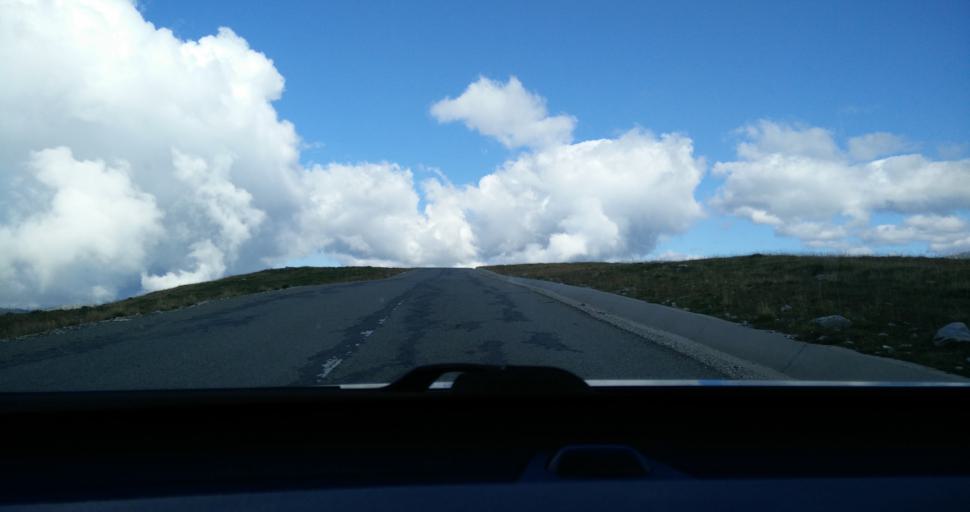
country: RO
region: Gorj
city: Novaci-Straini
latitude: 45.2601
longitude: 23.6936
